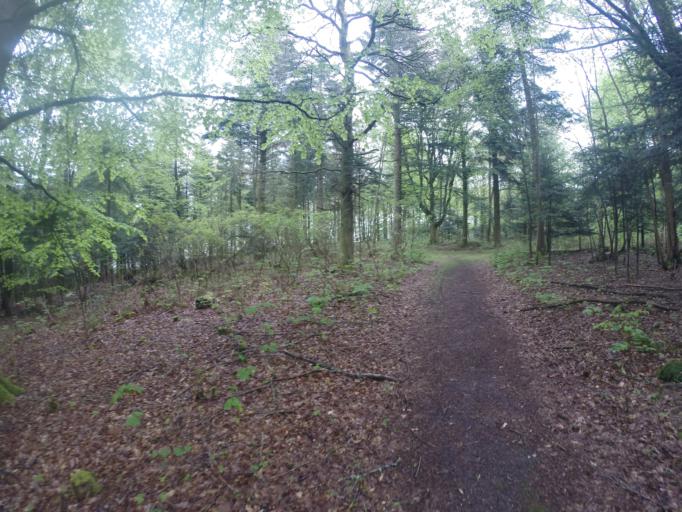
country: DK
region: North Denmark
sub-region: Thisted Kommune
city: Hanstholm
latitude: 57.0306
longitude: 8.5922
